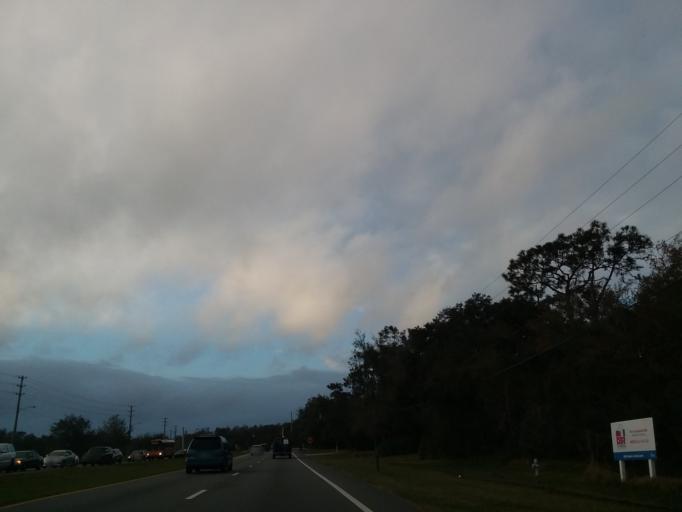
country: US
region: Florida
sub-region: Osceola County
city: Poinciana
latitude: 28.1979
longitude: -81.4401
